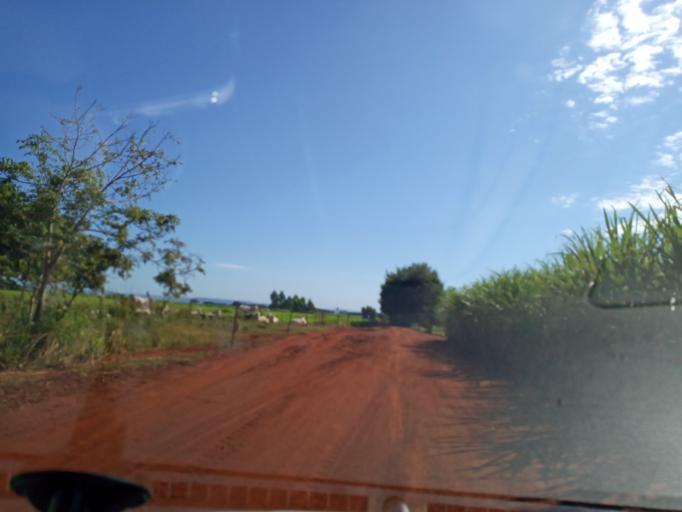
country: BR
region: Goias
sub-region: Itumbiara
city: Itumbiara
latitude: -18.4621
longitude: -49.1204
